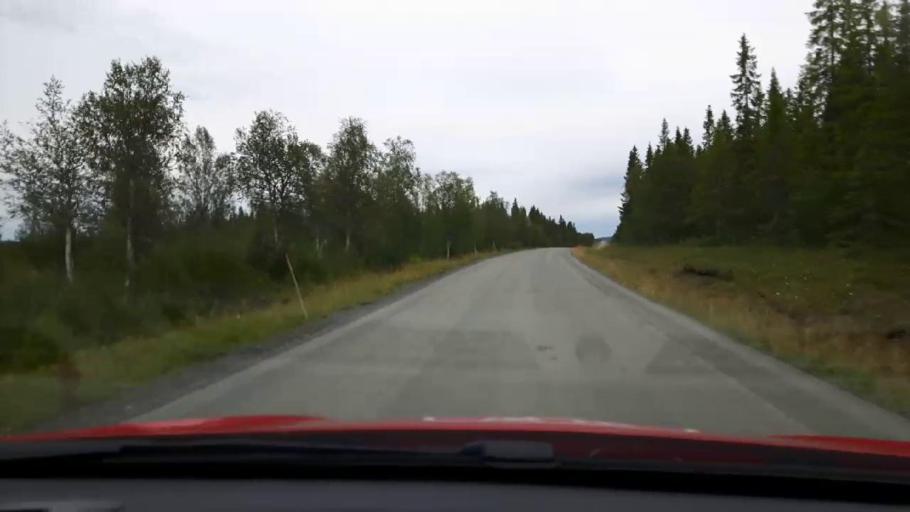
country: SE
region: Jaemtland
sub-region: Are Kommun
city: Are
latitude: 63.4509
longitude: 13.2124
